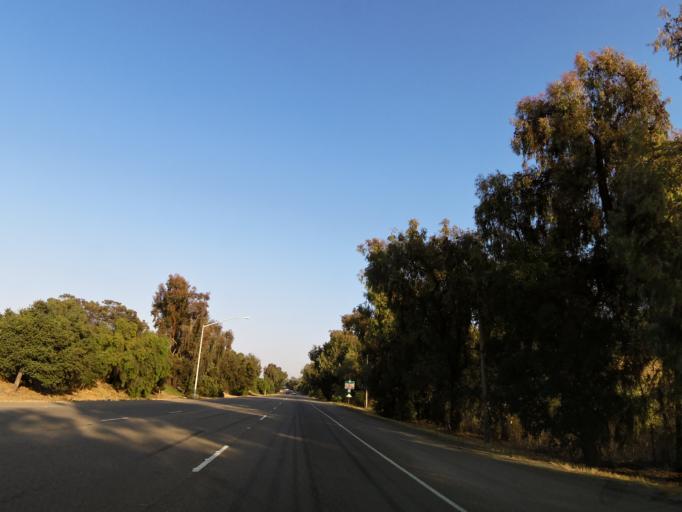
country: US
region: California
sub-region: San Luis Obispo County
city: Arroyo Grande
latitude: 35.1153
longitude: -120.5723
